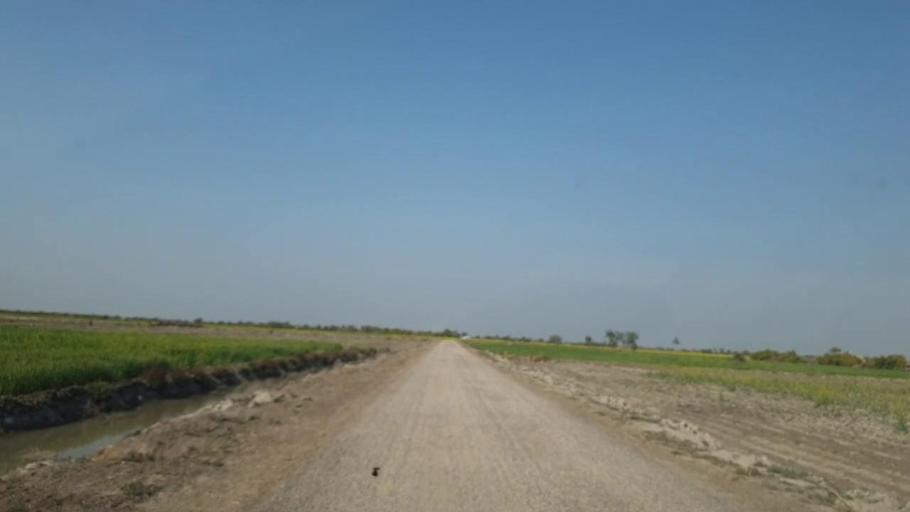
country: PK
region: Sindh
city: Mirpur Khas
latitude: 25.7336
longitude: 69.1614
